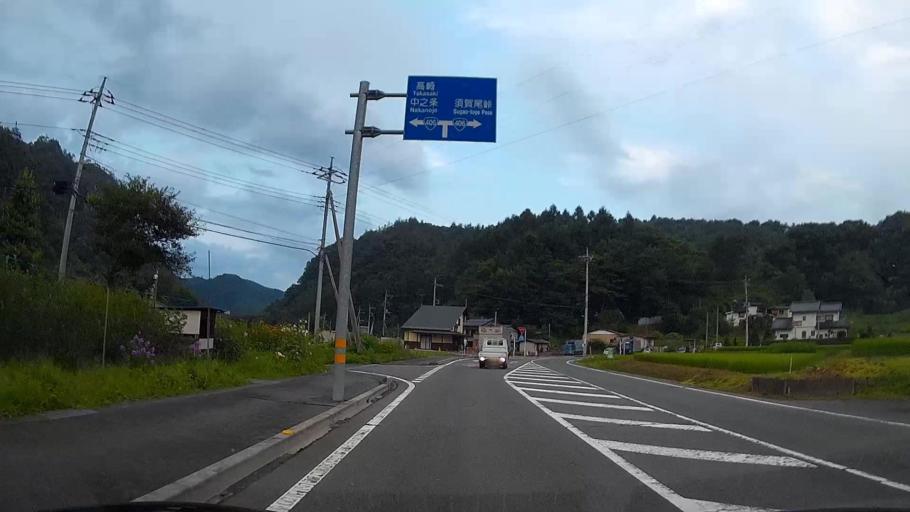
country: JP
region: Gunma
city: Nakanojomachi
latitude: 36.5137
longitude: 138.7638
